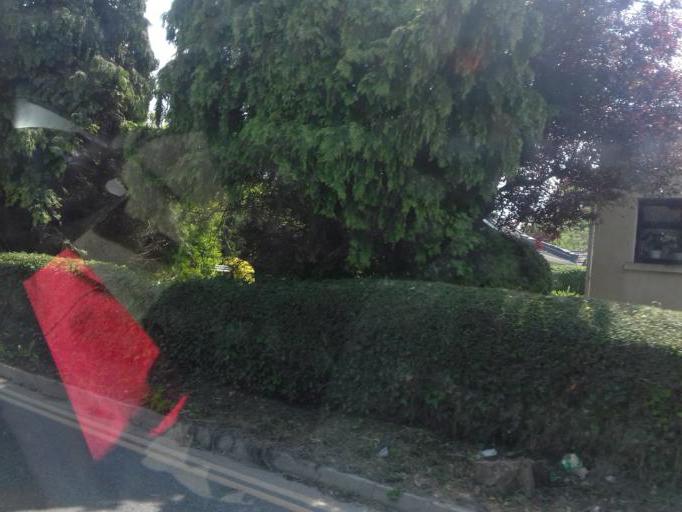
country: IE
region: Leinster
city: Donabate
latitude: 53.4925
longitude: -6.1346
